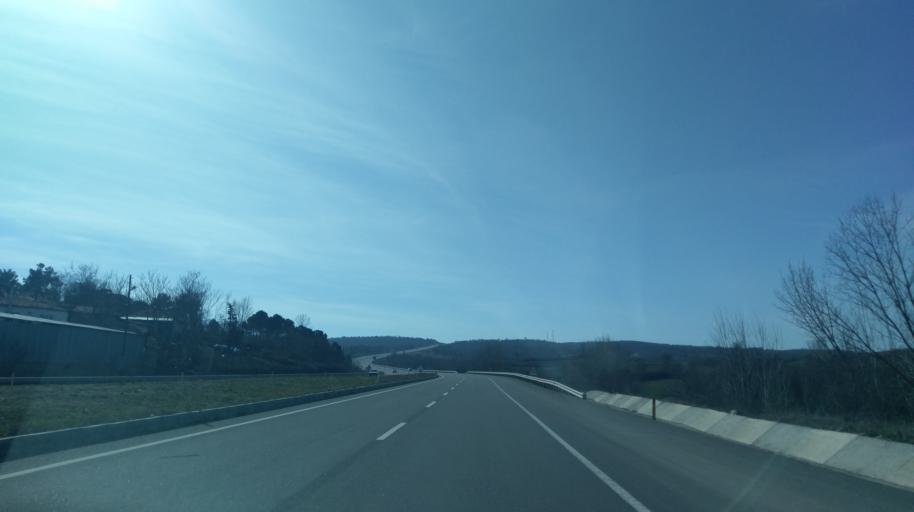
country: TR
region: Edirne
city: Kesan
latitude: 40.9899
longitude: 26.6371
